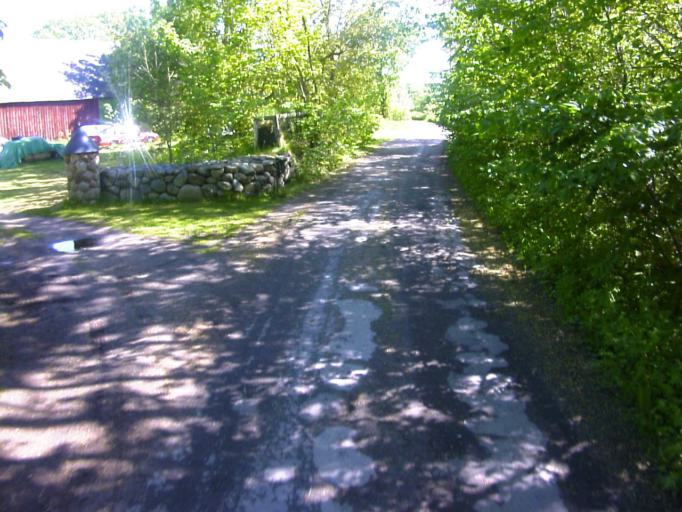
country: SE
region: Blekinge
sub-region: Solvesborgs Kommun
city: Soelvesborg
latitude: 56.0600
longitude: 14.6233
